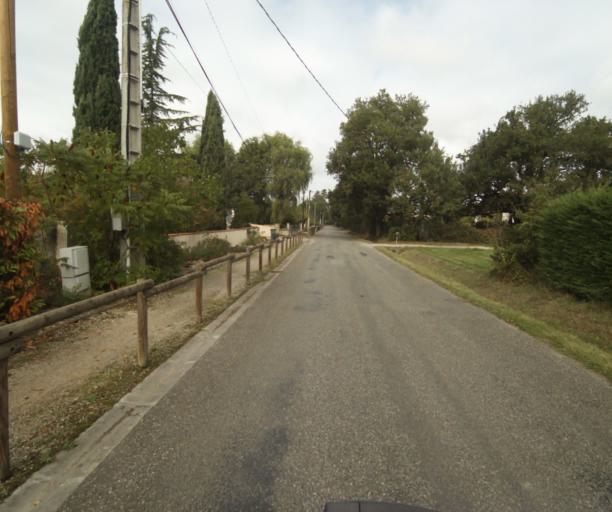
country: FR
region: Midi-Pyrenees
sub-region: Departement du Tarn-et-Garonne
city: Montech
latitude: 43.9541
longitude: 1.2483
